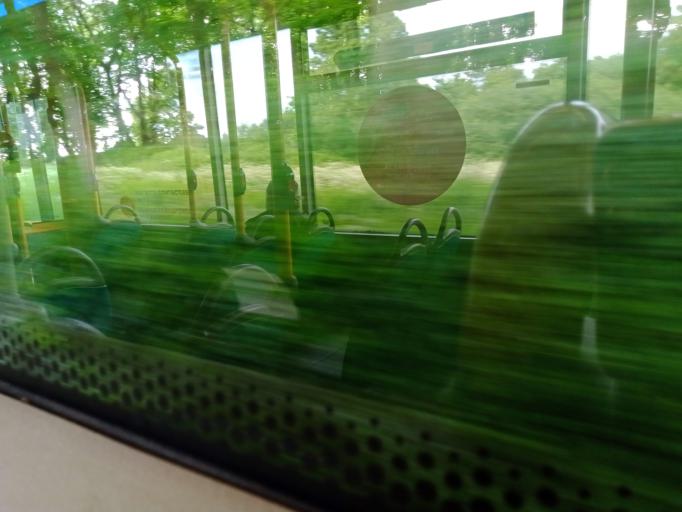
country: GB
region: Wales
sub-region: Anglesey
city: Llangoed
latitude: 53.2905
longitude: -4.0742
